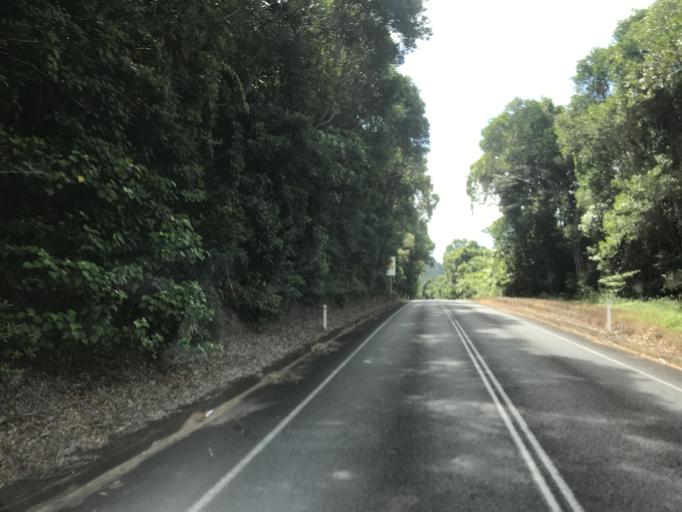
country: AU
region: Queensland
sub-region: Cassowary Coast
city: Innisfail
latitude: -17.8492
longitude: 146.0595
